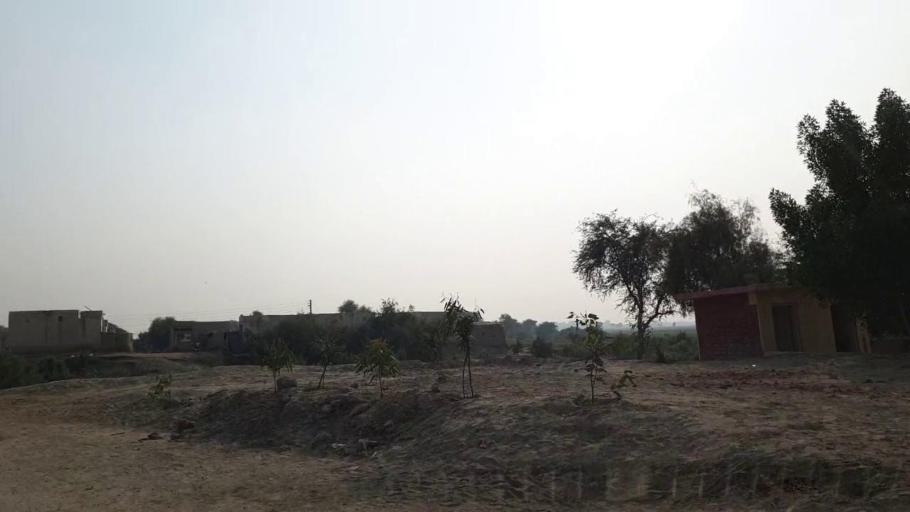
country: PK
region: Sindh
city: Bhan
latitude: 26.4579
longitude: 67.7279
